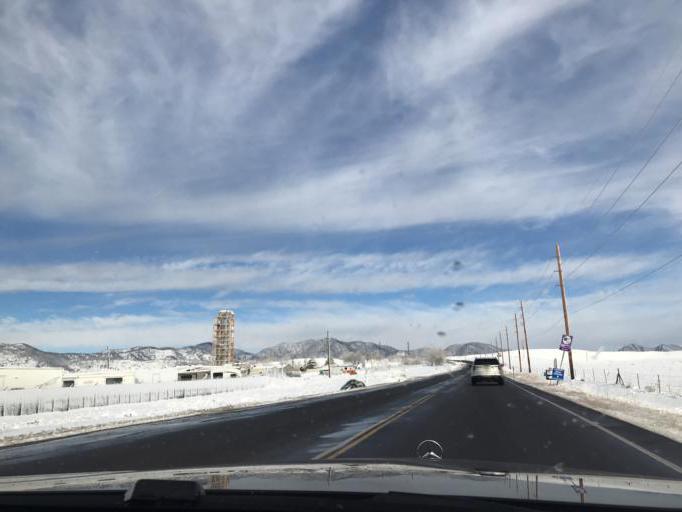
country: US
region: Colorado
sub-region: Boulder County
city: Superior
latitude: 39.8592
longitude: -105.1931
